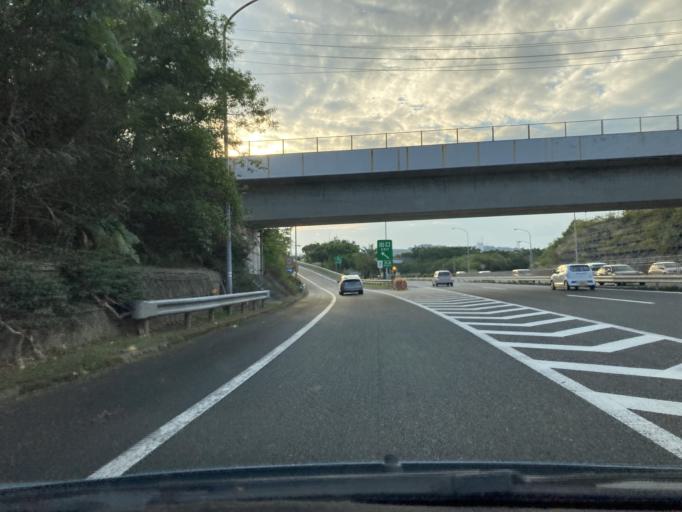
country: JP
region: Okinawa
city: Ginowan
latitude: 26.2486
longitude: 127.7524
